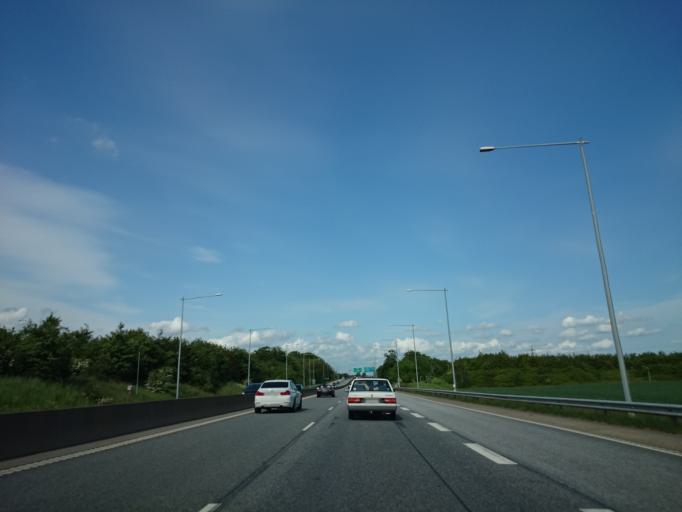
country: SE
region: Skane
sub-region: Burlovs Kommun
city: Arloev
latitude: 55.6349
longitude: 13.0924
